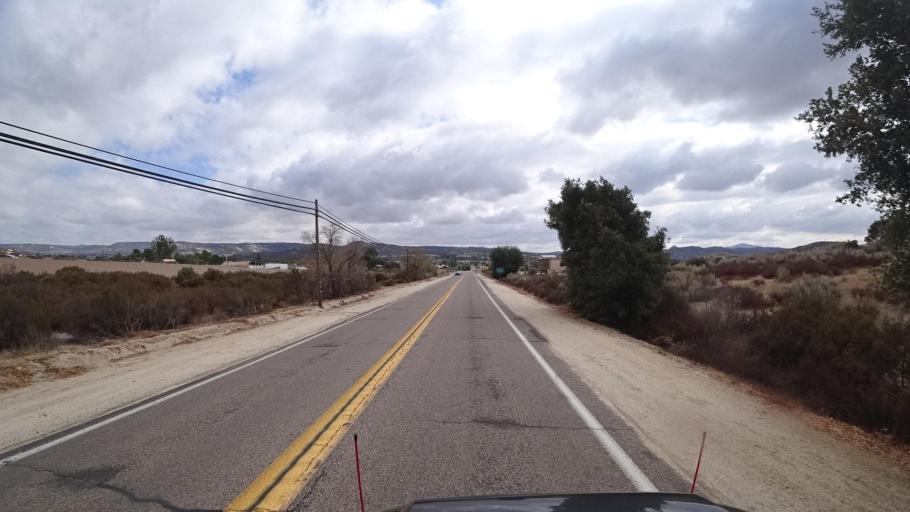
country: US
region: California
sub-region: San Diego County
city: Campo
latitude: 32.6318
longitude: -116.4741
